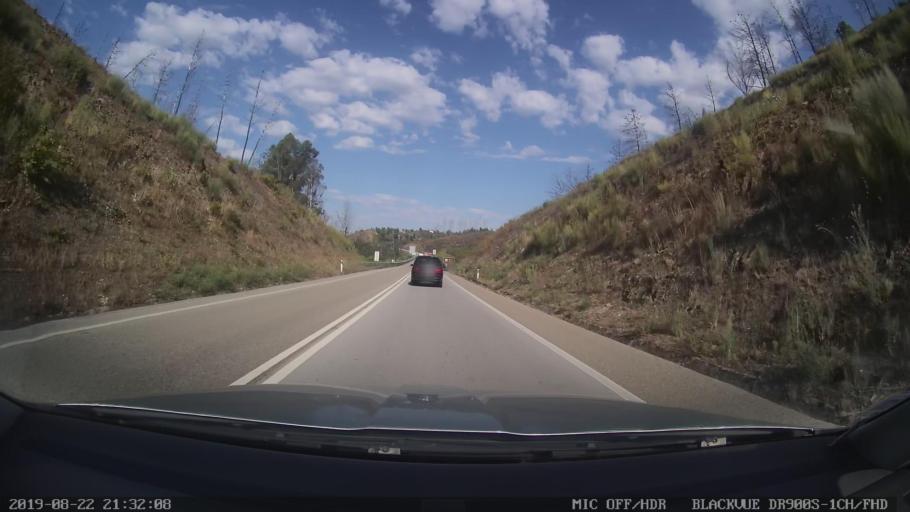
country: PT
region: Leiria
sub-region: Pedrogao Grande
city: Pedrogao Grande
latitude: 39.9258
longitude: -8.1606
